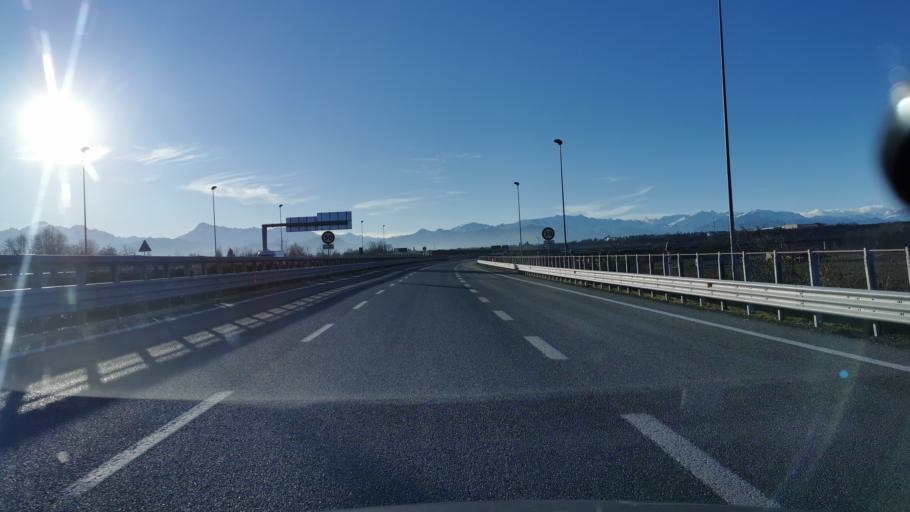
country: IT
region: Piedmont
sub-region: Provincia di Cuneo
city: Cuneo
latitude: 44.4233
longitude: 7.5854
